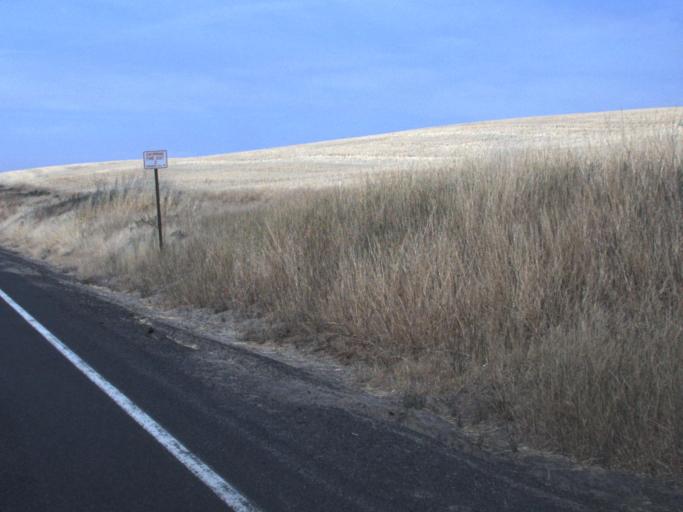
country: US
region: Idaho
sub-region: Benewah County
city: Plummer
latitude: 47.3228
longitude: -117.1815
